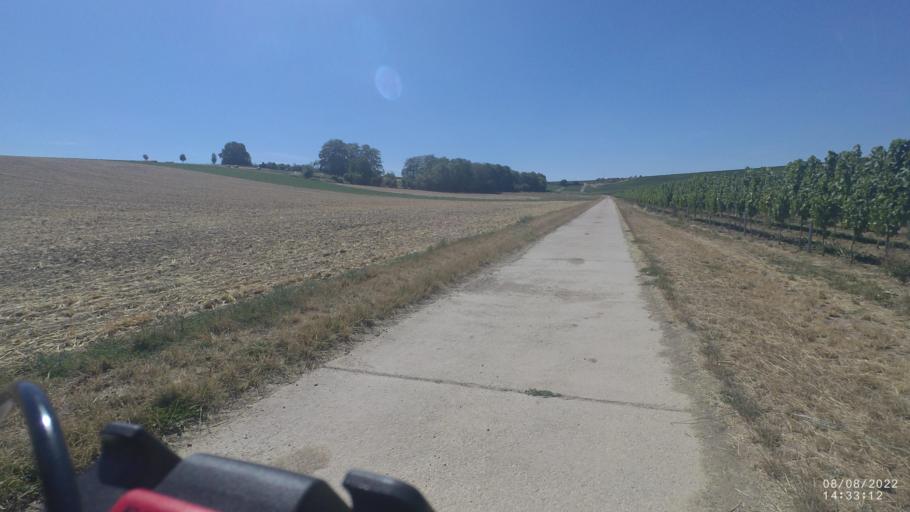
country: DE
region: Rheinland-Pfalz
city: Ober-Saulheim
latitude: 49.8728
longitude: 8.1223
